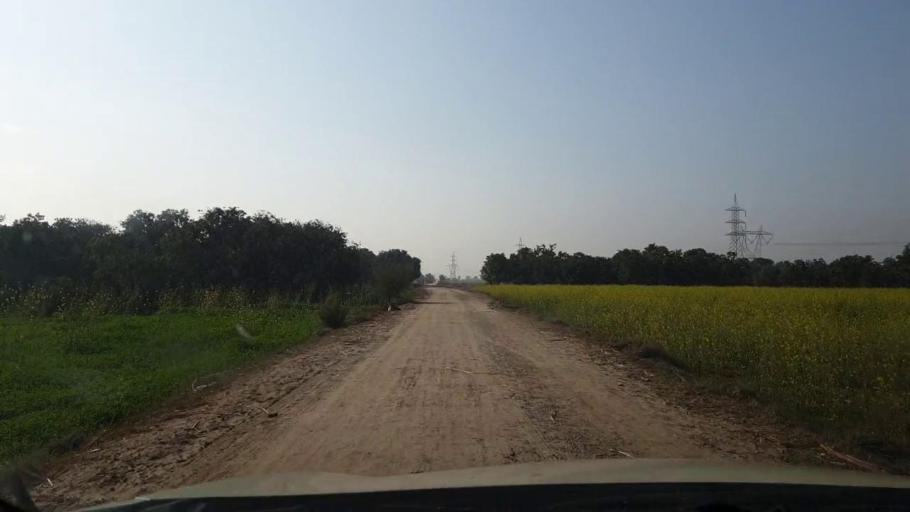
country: PK
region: Sindh
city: Bhit Shah
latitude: 25.6950
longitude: 68.5429
